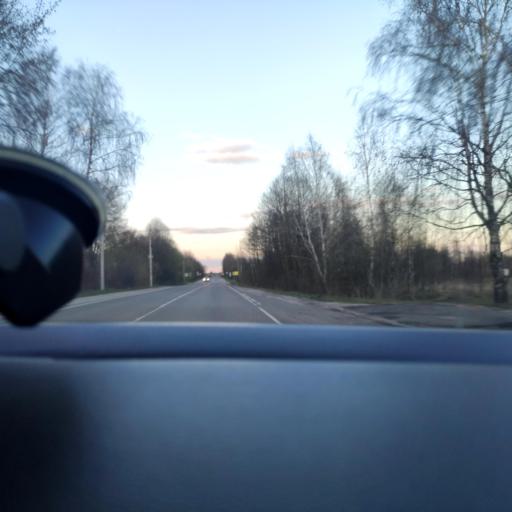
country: RU
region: Moskovskaya
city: Krasnyy Tkach
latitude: 55.4286
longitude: 39.2038
